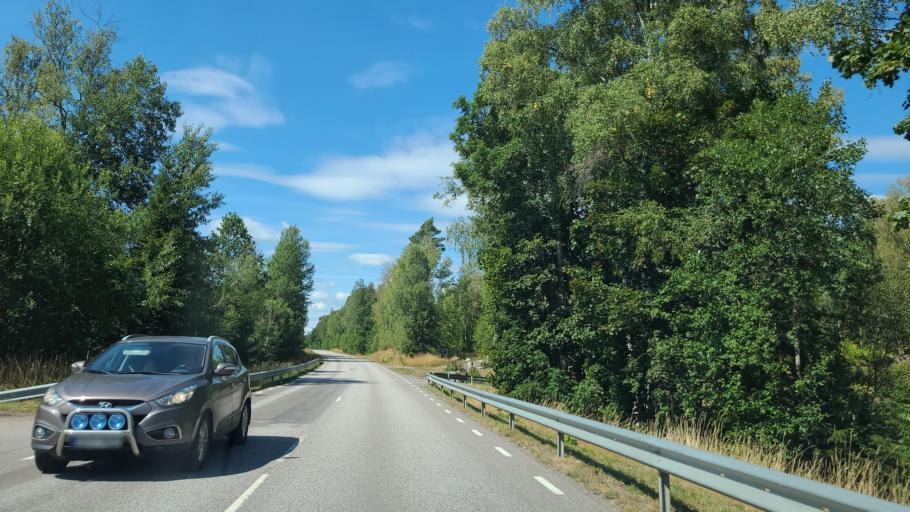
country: SE
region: Kalmar
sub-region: Emmaboda Kommun
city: Emmaboda
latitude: 56.5566
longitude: 15.7378
